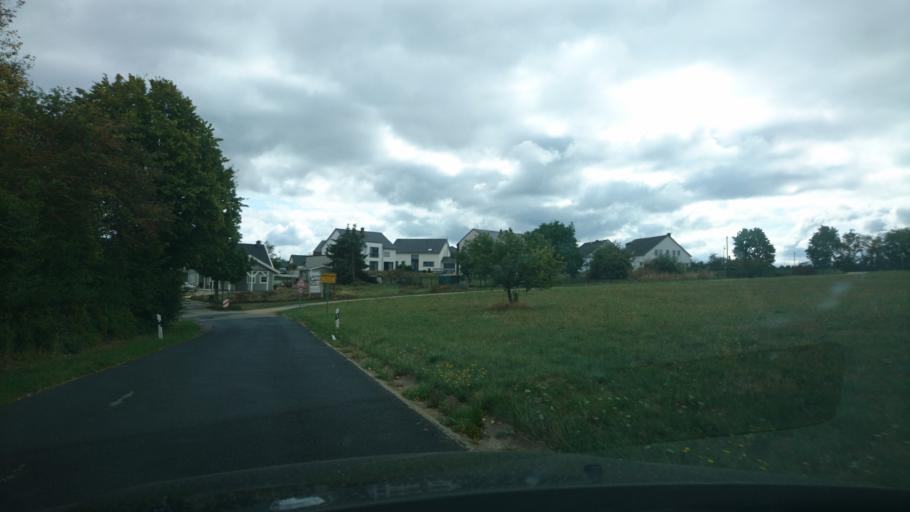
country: DE
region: Rheinland-Pfalz
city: Wiltingen
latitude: 49.6833
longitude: 6.6024
